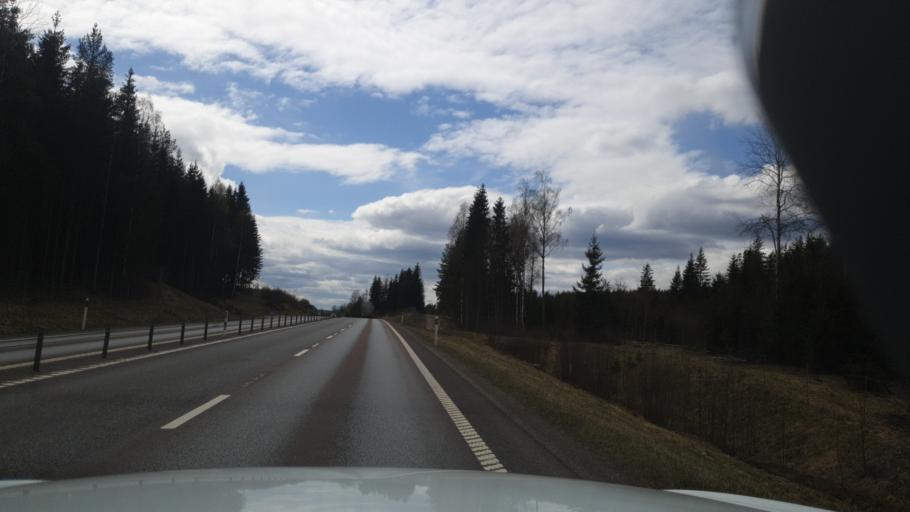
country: SE
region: Vaermland
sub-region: Arvika Kommun
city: Arvika
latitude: 59.6556
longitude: 12.7558
